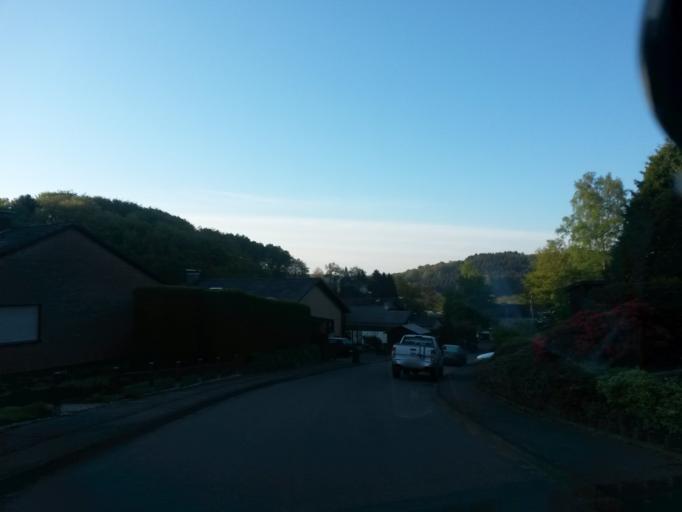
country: DE
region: North Rhine-Westphalia
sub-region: Regierungsbezirk Arnsberg
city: Herscheid
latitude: 51.1216
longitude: 7.7622
